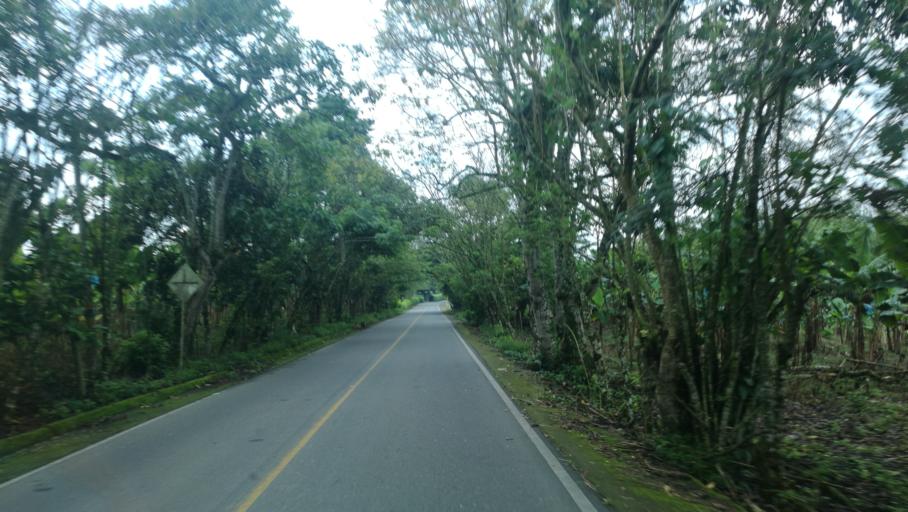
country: CO
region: Quindio
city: Montenegro
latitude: 4.5093
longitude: -75.7678
